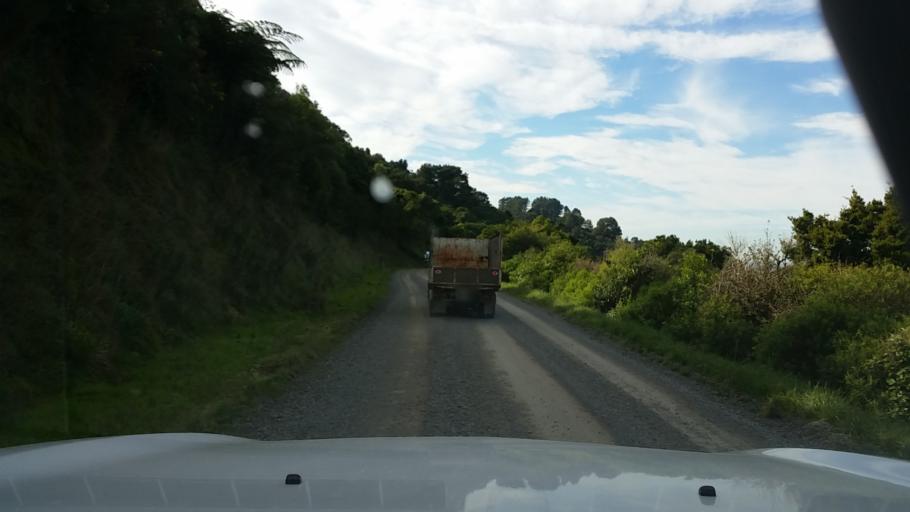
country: NZ
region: Wellington
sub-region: Masterton District
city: Masterton
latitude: -41.0389
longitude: 175.4144
